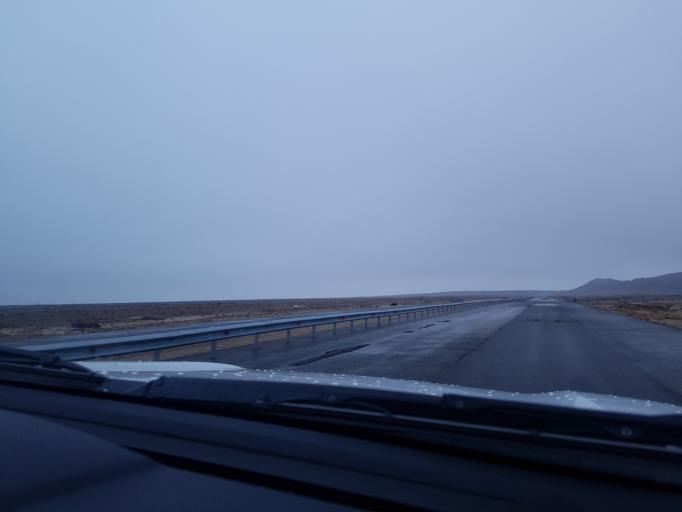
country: TM
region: Balkan
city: Balkanabat
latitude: 39.9114
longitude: 53.9122
